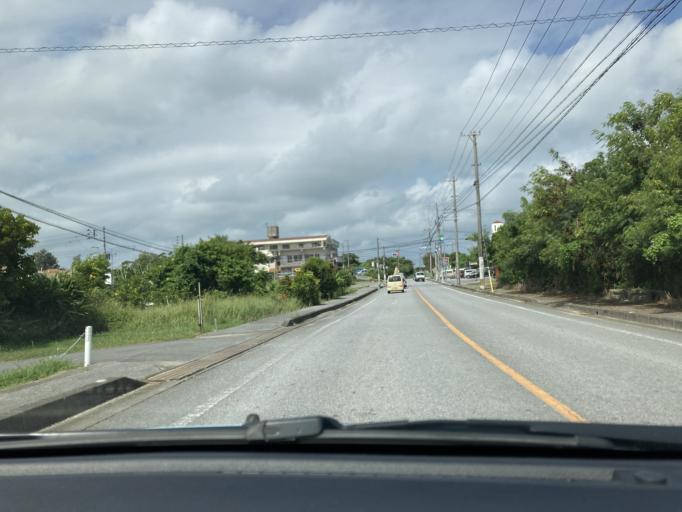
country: JP
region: Okinawa
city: Ishikawa
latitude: 26.3979
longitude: 127.8483
